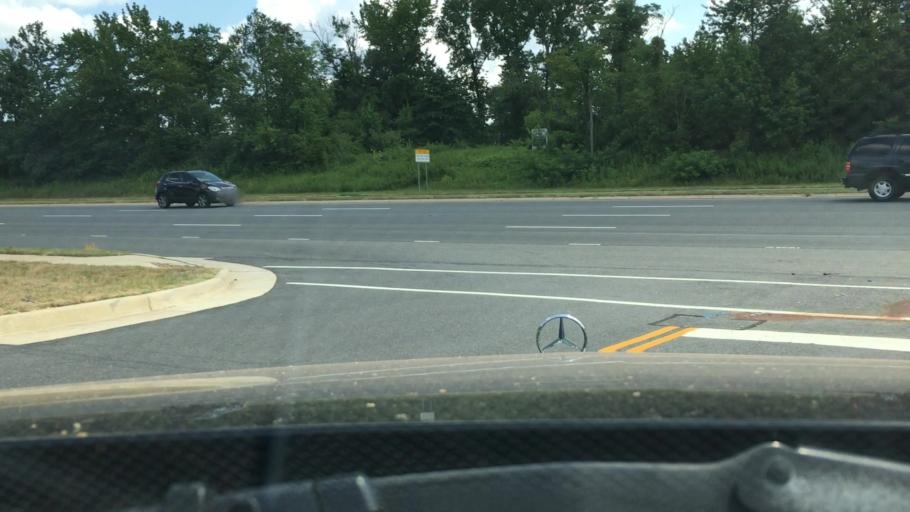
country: US
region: Virginia
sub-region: Spotsylvania County
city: Spotsylvania
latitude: 38.2909
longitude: -77.5590
